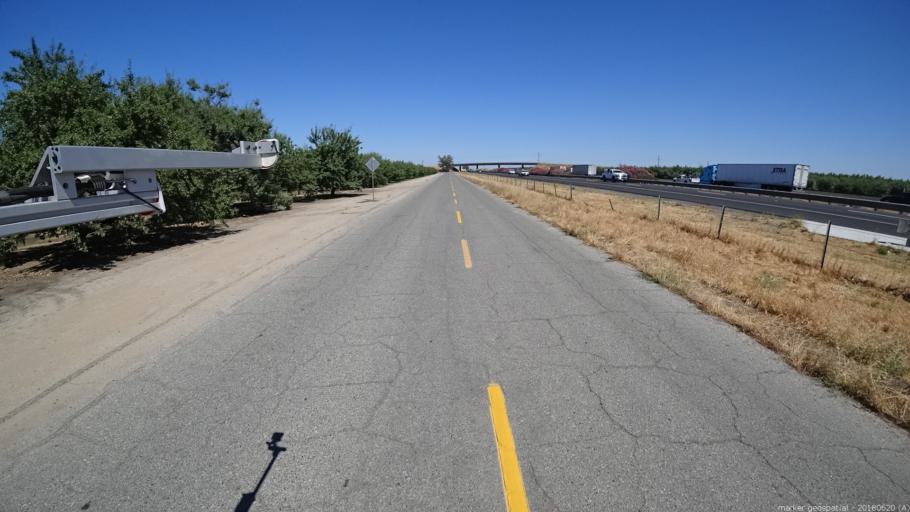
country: US
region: California
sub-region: Madera County
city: Parksdale
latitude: 36.9063
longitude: -120.0033
